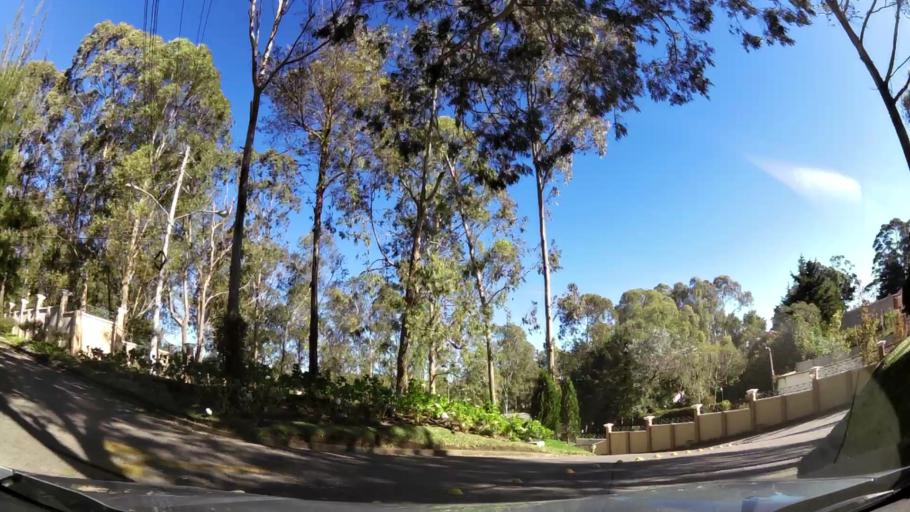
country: GT
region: Guatemala
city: Fraijanes
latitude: 14.5058
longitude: -90.4639
